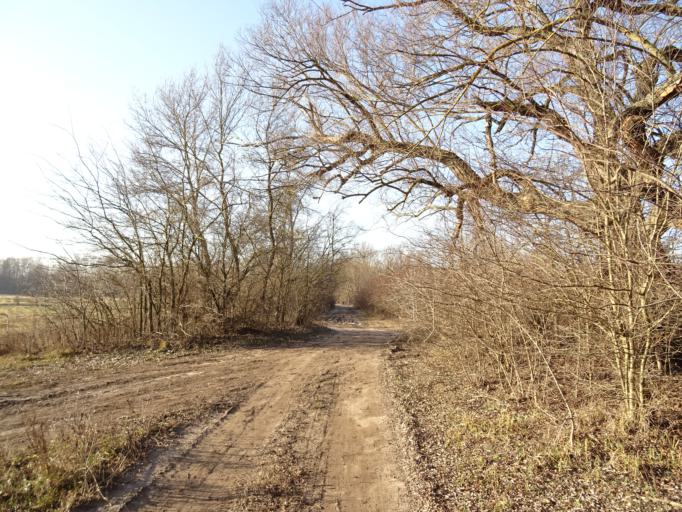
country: HU
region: Pest
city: Tapiosag
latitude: 47.4236
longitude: 19.6463
